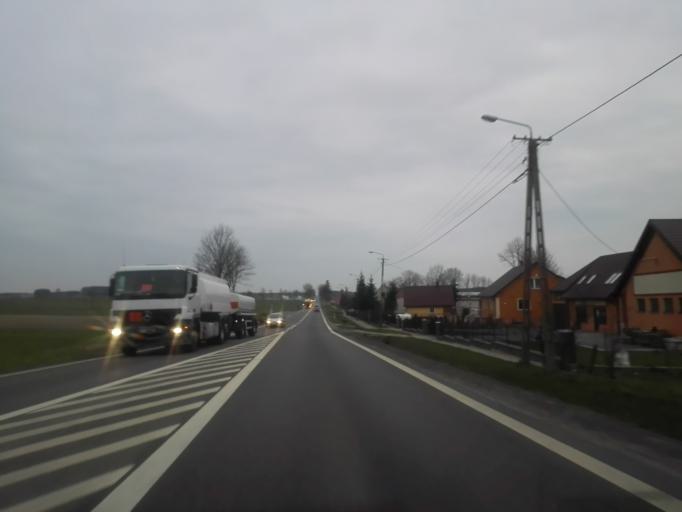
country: PL
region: Podlasie
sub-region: Powiat kolnenski
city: Stawiski
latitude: 53.4651
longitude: 22.2000
